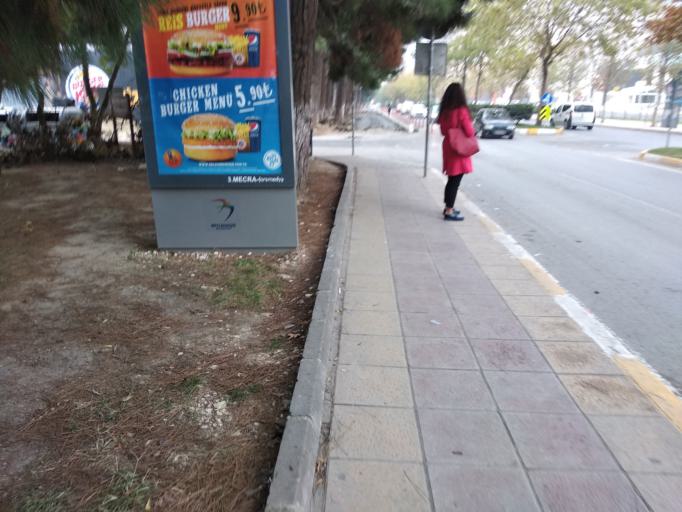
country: TR
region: Istanbul
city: Beylikduezue
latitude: 41.0119
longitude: 28.6443
